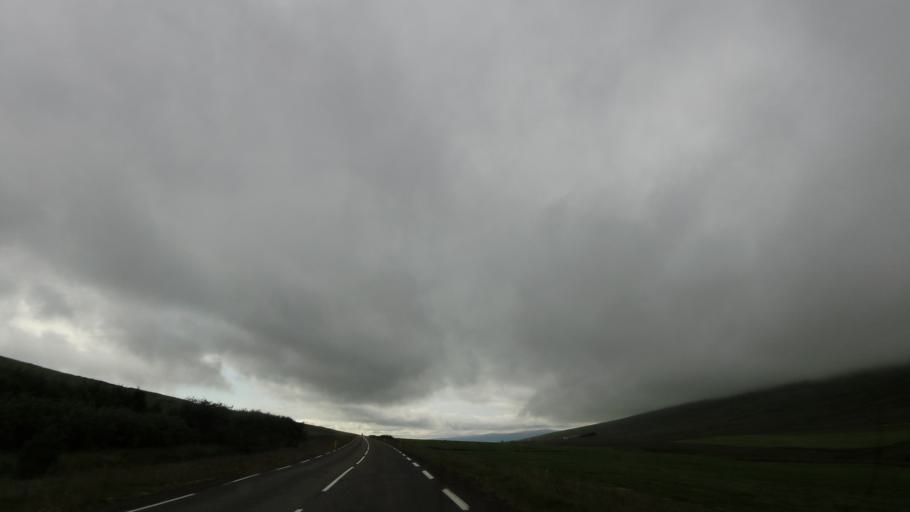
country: IS
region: Northeast
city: Laugar
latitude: 65.7807
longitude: -17.5809
